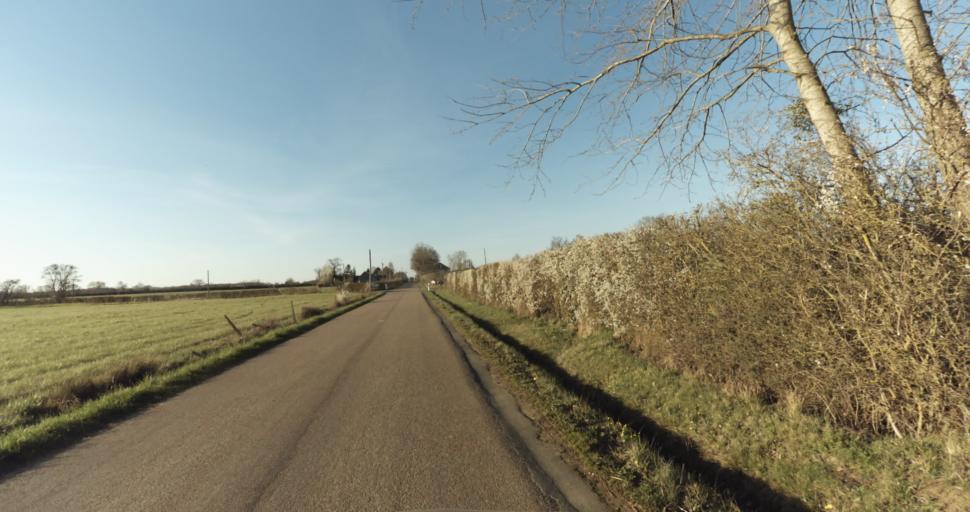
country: FR
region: Lower Normandy
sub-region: Departement du Calvados
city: Saint-Pierre-sur-Dives
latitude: 48.9675
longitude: -0.0048
